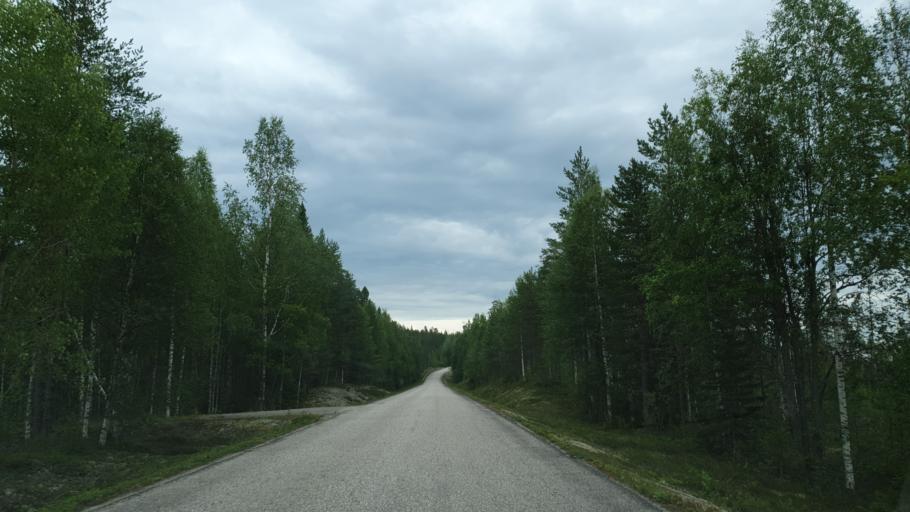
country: FI
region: Kainuu
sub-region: Kehys-Kainuu
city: Kuhmo
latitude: 64.3389
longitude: 29.3307
